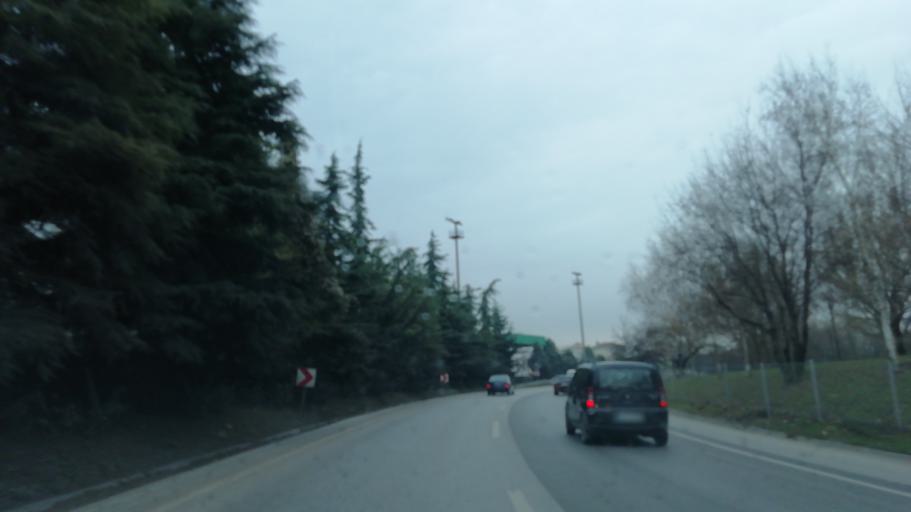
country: TR
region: Kocaeli
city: Izmit
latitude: 40.7636
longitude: 29.8755
